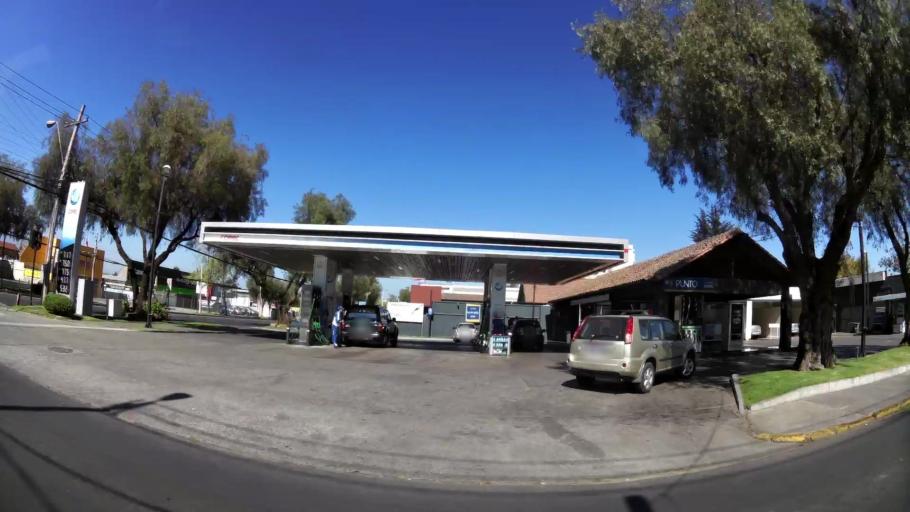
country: CL
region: Santiago Metropolitan
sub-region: Provincia de Santiago
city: Villa Presidente Frei, Nunoa, Santiago, Chile
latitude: -33.3981
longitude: -70.5518
